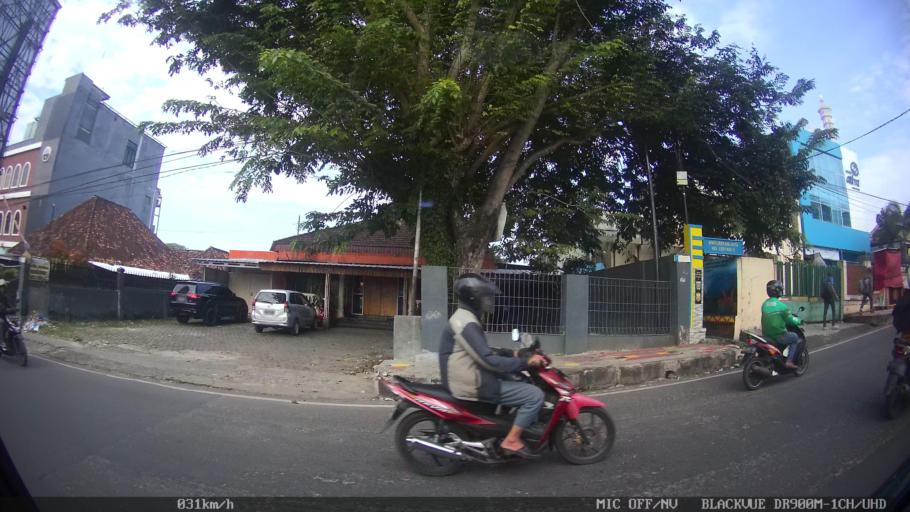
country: ID
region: Lampung
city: Bandarlampung
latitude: -5.4313
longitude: 105.2617
